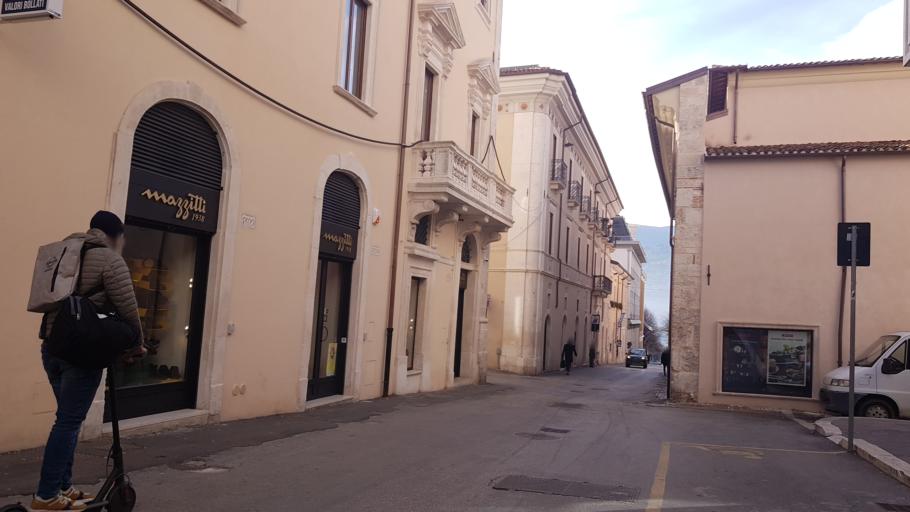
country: IT
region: Abruzzo
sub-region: Provincia dell' Aquila
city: L'Aquila
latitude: 42.3478
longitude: 13.3984
